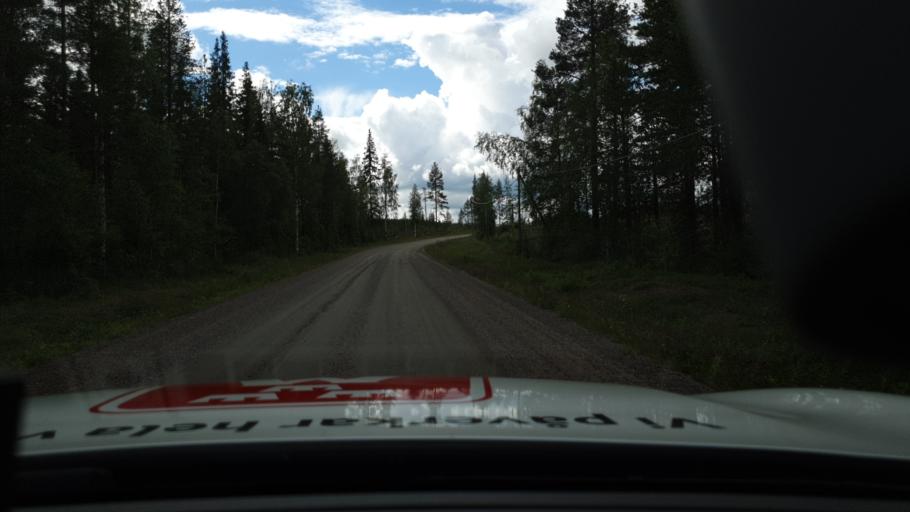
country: SE
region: Norrbotten
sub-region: Alvsbyns Kommun
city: AElvsbyn
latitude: 66.2857
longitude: 21.1520
